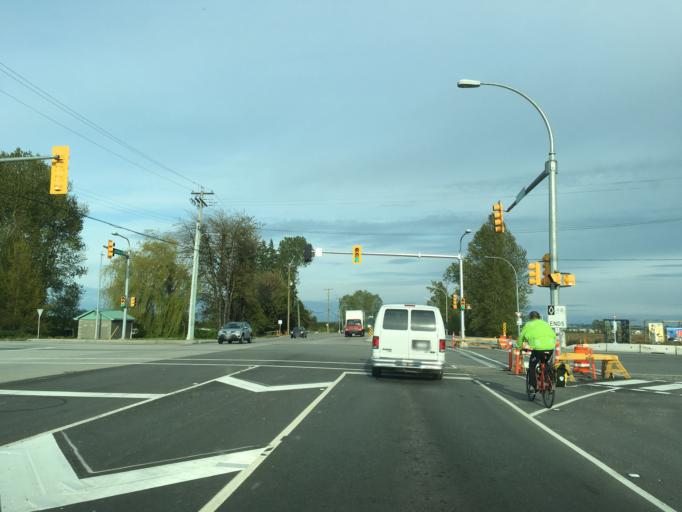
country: CA
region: British Columbia
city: Ladner
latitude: 49.1698
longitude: -123.0135
